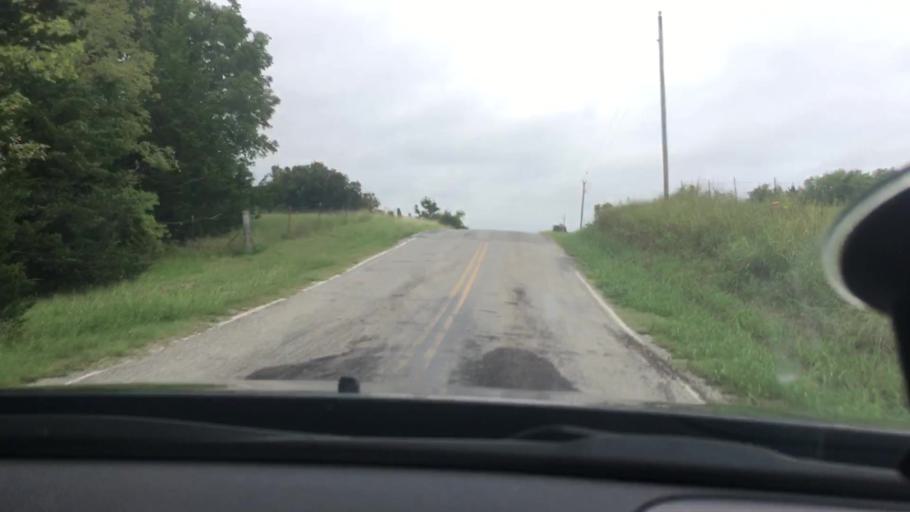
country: US
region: Oklahoma
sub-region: Pontotoc County
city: Byng
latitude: 34.8045
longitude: -96.5475
